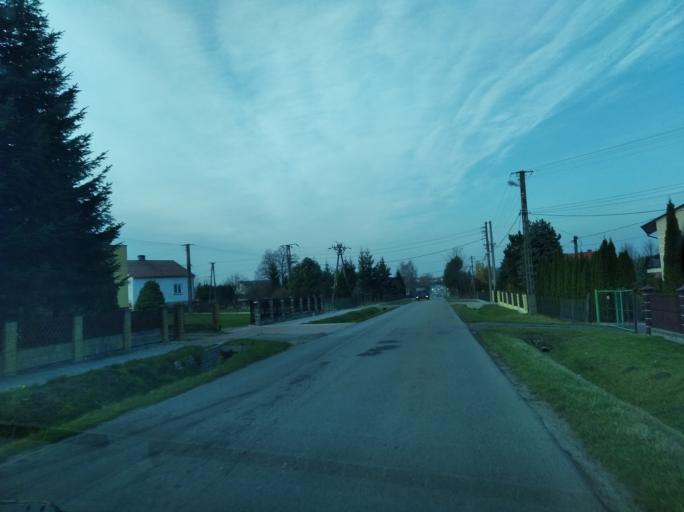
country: PL
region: Subcarpathian Voivodeship
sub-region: Powiat ropczycko-sedziszowski
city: Sedziszow Malopolski
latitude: 50.0604
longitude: 21.7345
